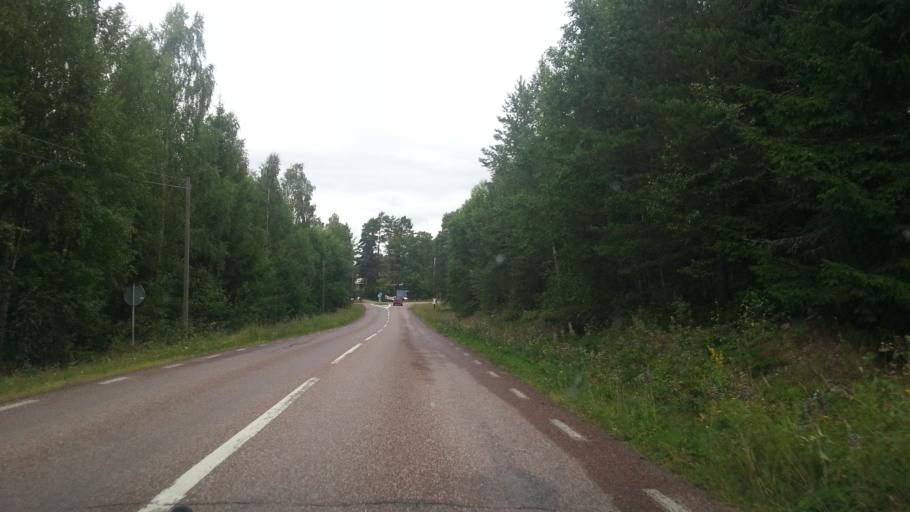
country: SE
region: Dalarna
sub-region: Faluns Kommun
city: Svardsjo
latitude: 60.6515
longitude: 15.7857
